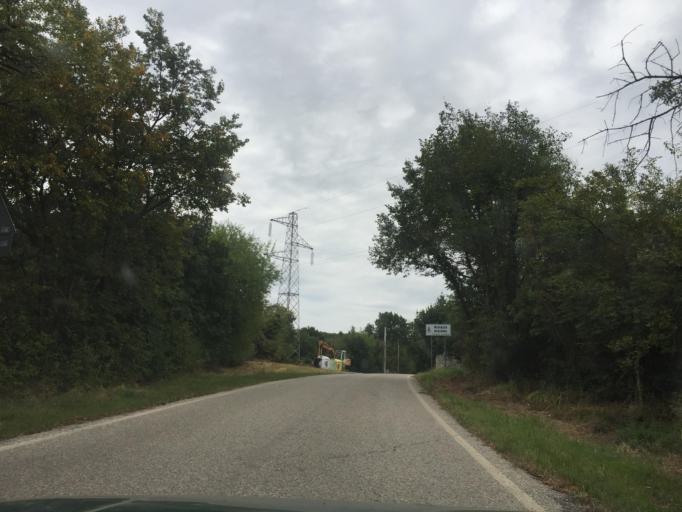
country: IT
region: Friuli Venezia Giulia
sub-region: Provincia di Trieste
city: Duino
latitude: 45.7952
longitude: 13.6014
